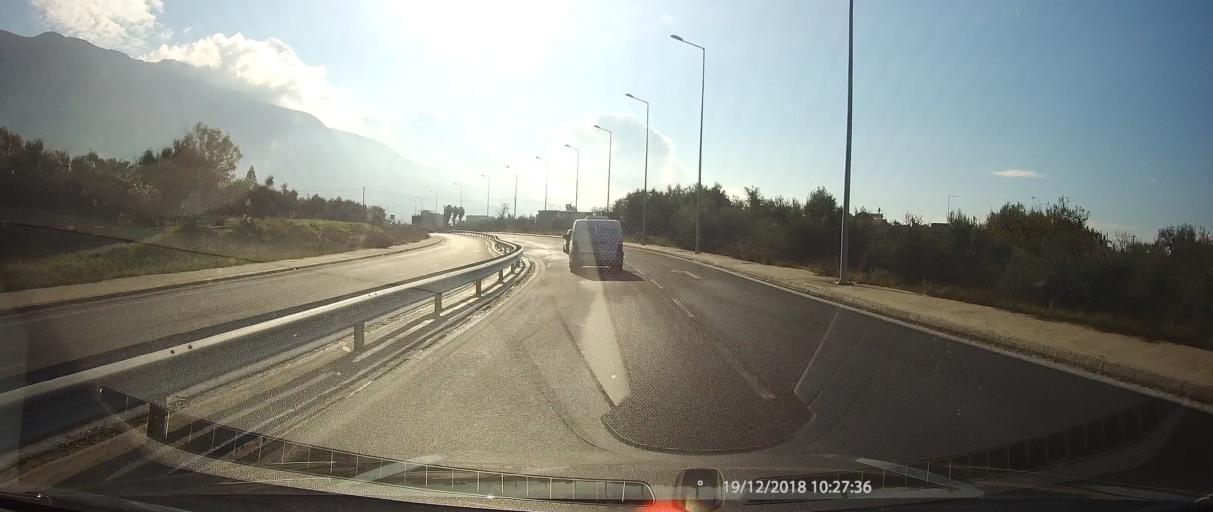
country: GR
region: Peloponnese
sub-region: Nomos Messinias
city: Kalamata
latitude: 37.0327
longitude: 22.1357
